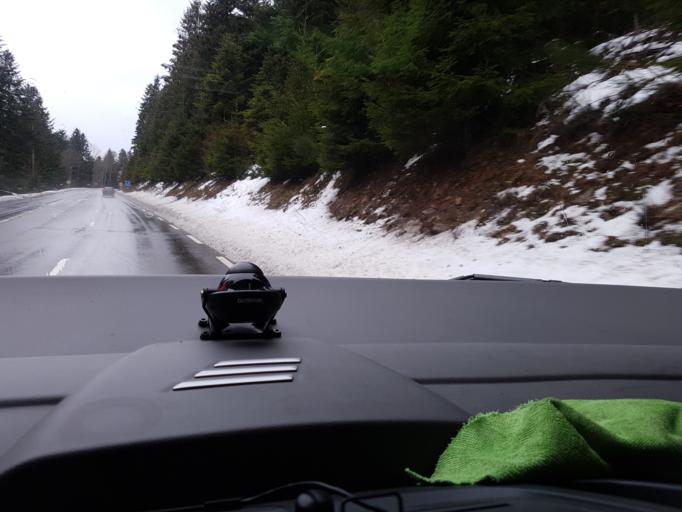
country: FR
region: Lorraine
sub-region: Departement des Vosges
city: Plainfaing
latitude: 48.1699
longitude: 7.0456
